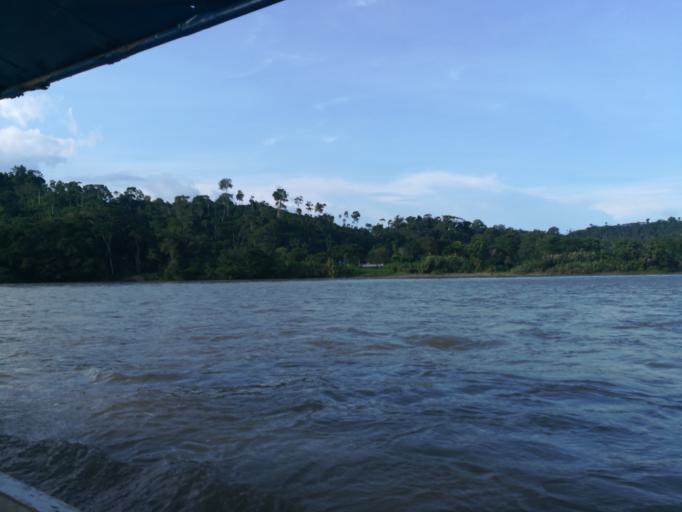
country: EC
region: Orellana
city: Boca Suno
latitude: -0.8809
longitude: -77.2879
